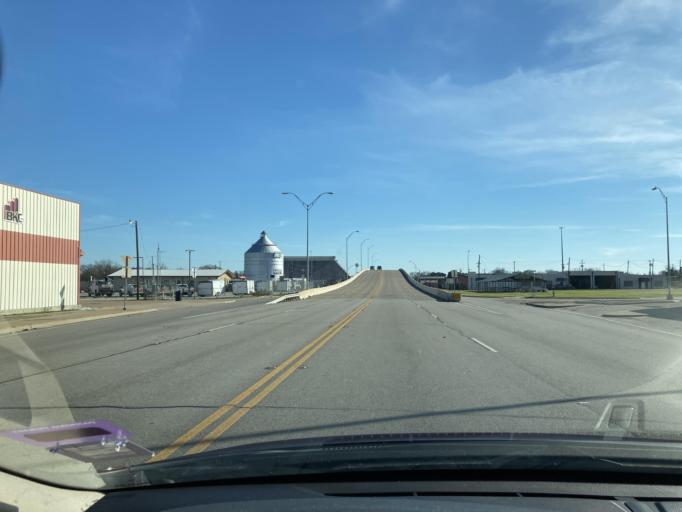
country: US
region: Texas
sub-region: Navarro County
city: Corsicana
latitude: 32.0958
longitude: -96.4606
